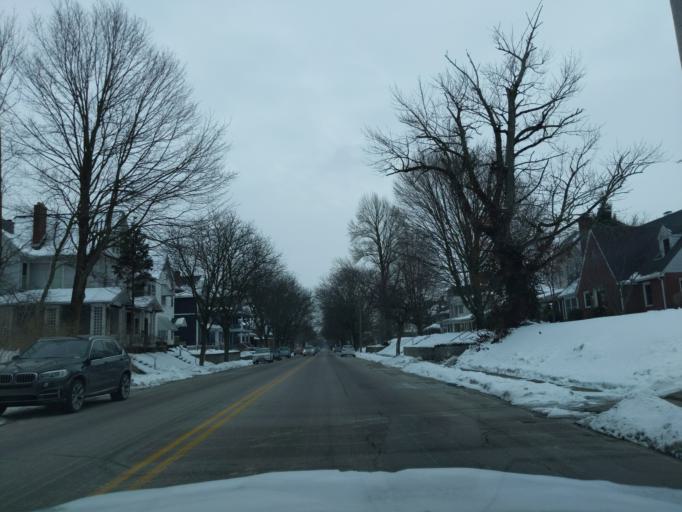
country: US
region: Indiana
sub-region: Tippecanoe County
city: Lafayette
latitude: 40.4124
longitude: -86.8866
